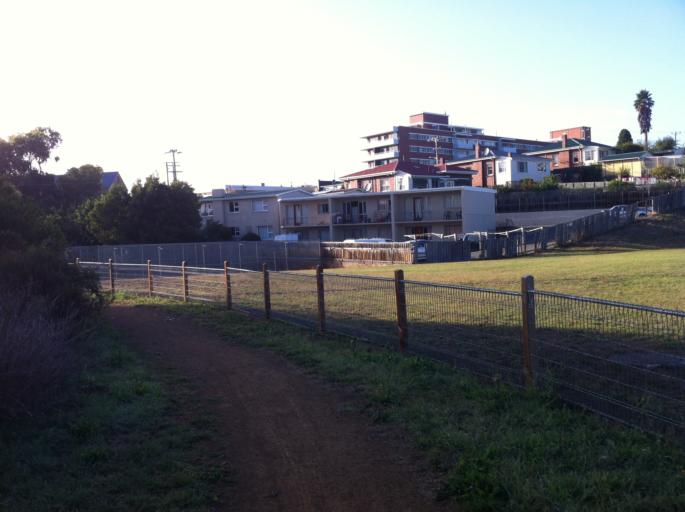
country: AU
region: Tasmania
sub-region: Glenorchy
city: Moonah
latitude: -42.8501
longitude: 147.3044
